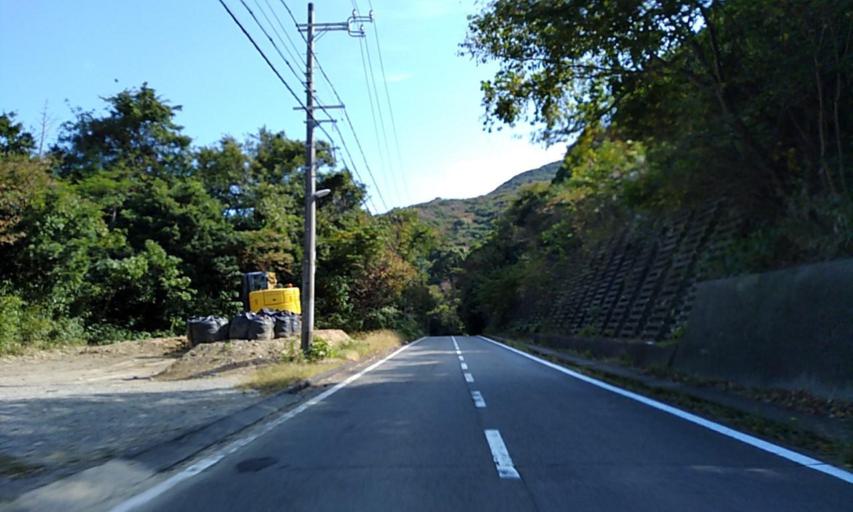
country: JP
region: Wakayama
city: Gobo
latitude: 33.9673
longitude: 135.0906
